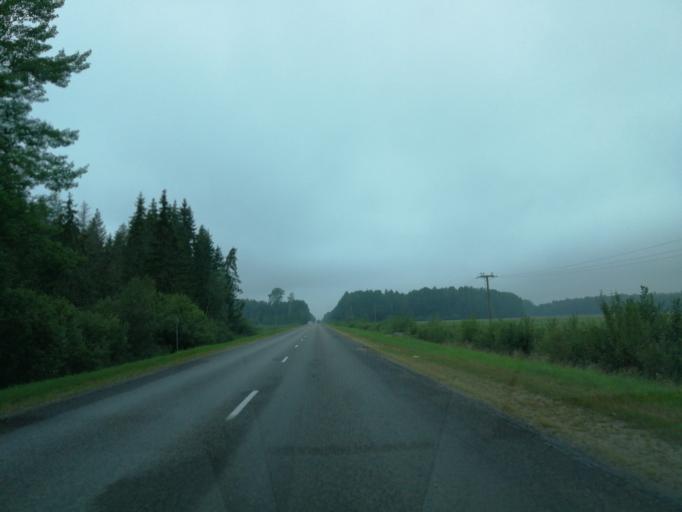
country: LV
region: Varkava
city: Vecvarkava
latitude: 56.3205
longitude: 26.4364
